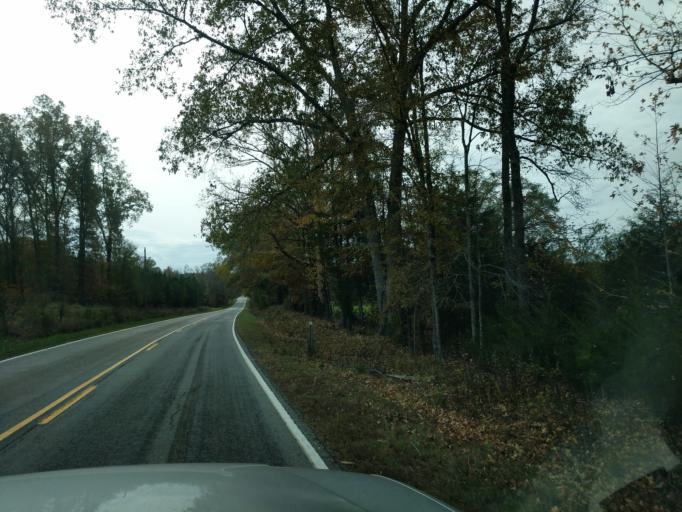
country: US
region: South Carolina
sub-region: Laurens County
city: Joanna
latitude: 34.2910
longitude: -81.8448
